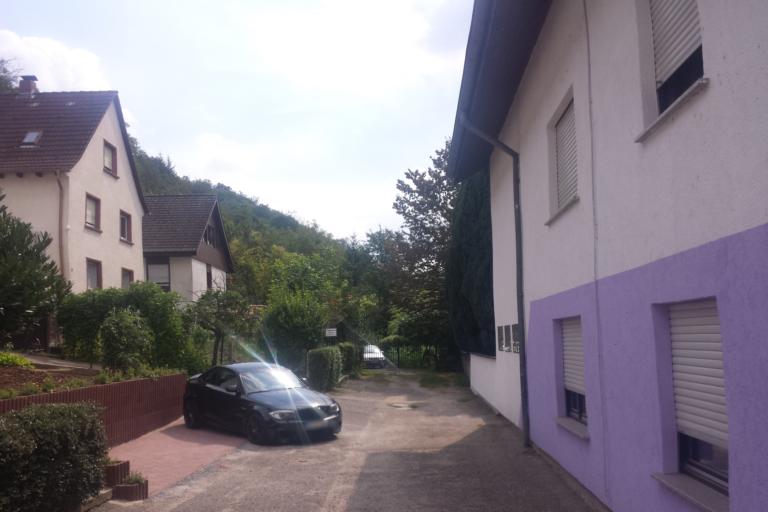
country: DE
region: Baden-Wuerttemberg
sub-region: Karlsruhe Region
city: Hemsbach
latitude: 49.5768
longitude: 8.6631
